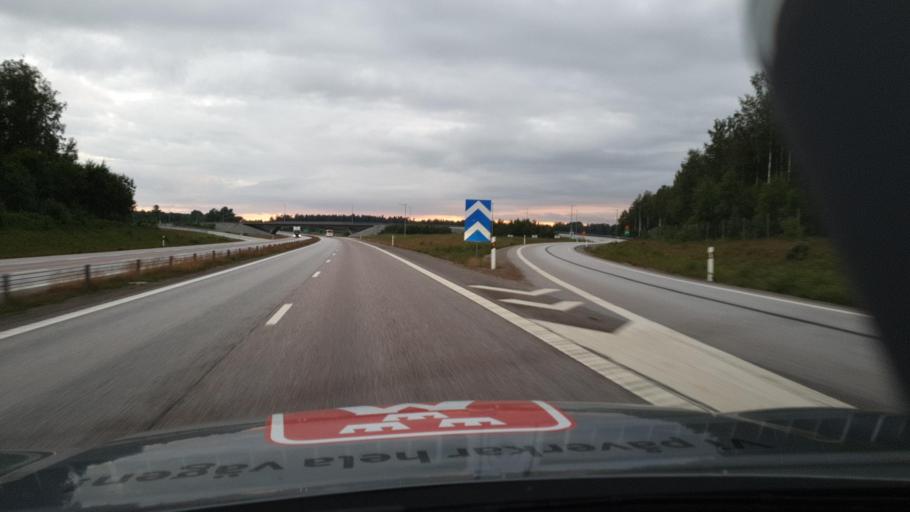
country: SE
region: OErebro
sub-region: Orebro Kommun
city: Vintrosa
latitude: 59.2479
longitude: 15.0618
